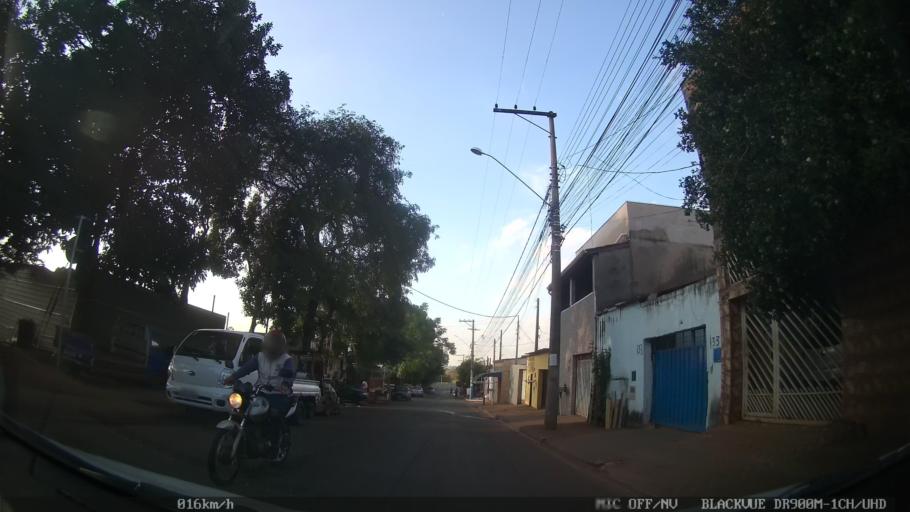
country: BR
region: Sao Paulo
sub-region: Hortolandia
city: Hortolandia
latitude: -22.8714
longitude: -47.1444
